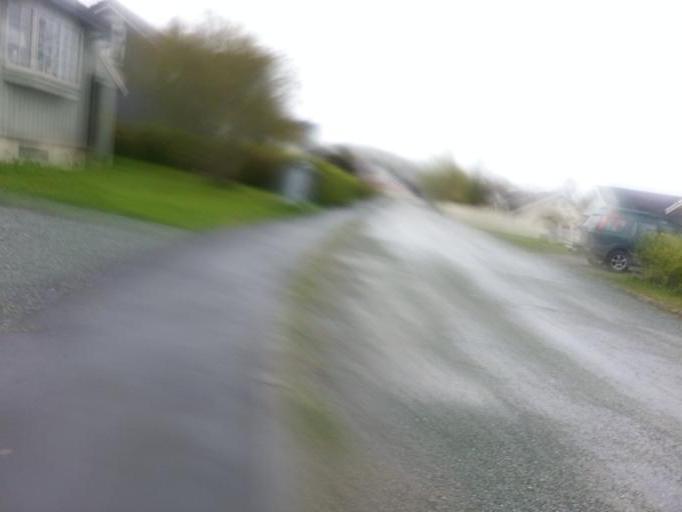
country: NO
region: Sor-Trondelag
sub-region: Trondheim
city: Trondheim
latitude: 63.3907
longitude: 10.3483
